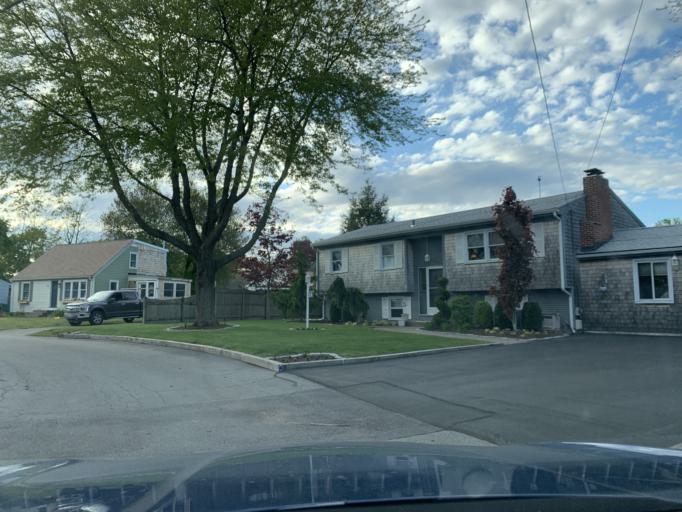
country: US
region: Rhode Island
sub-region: Kent County
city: Warwick
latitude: 41.6605
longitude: -71.4162
